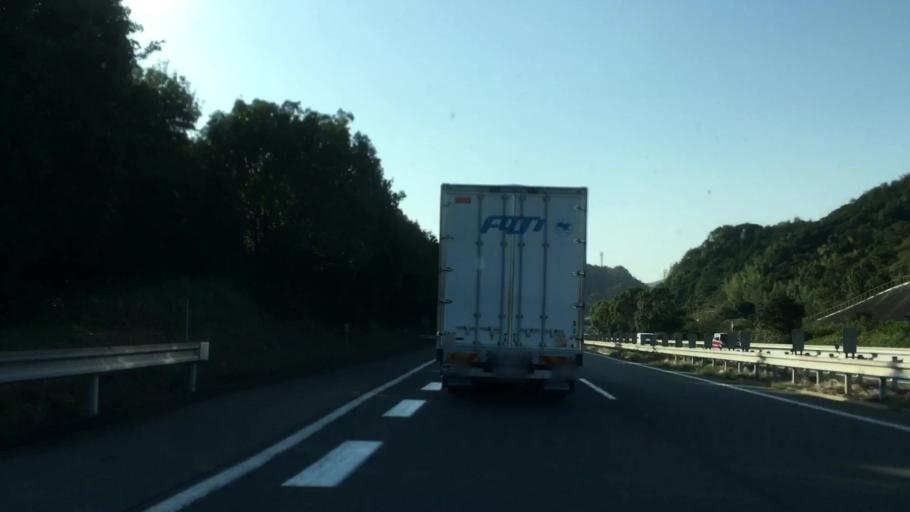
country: JP
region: Yamaguchi
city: Ogori-shimogo
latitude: 34.0857
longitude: 131.4691
